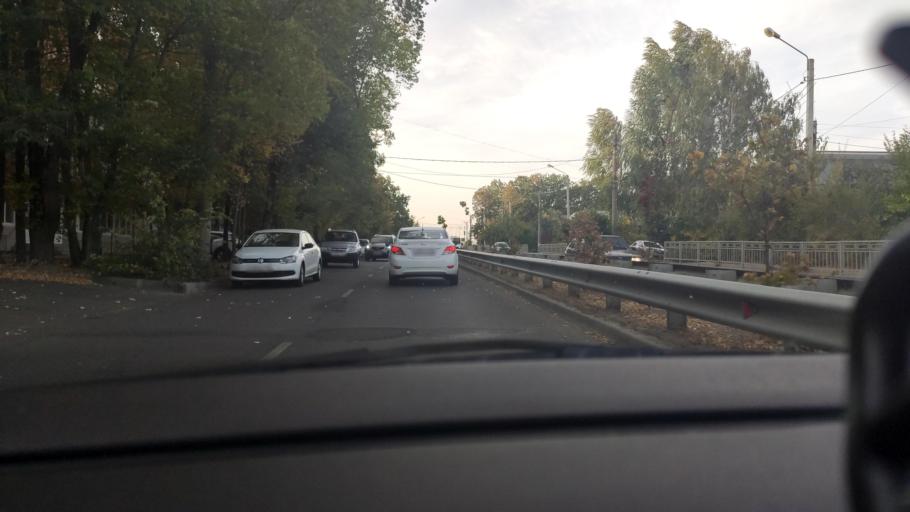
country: RU
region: Voronezj
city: Voronezh
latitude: 51.7028
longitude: 39.2308
